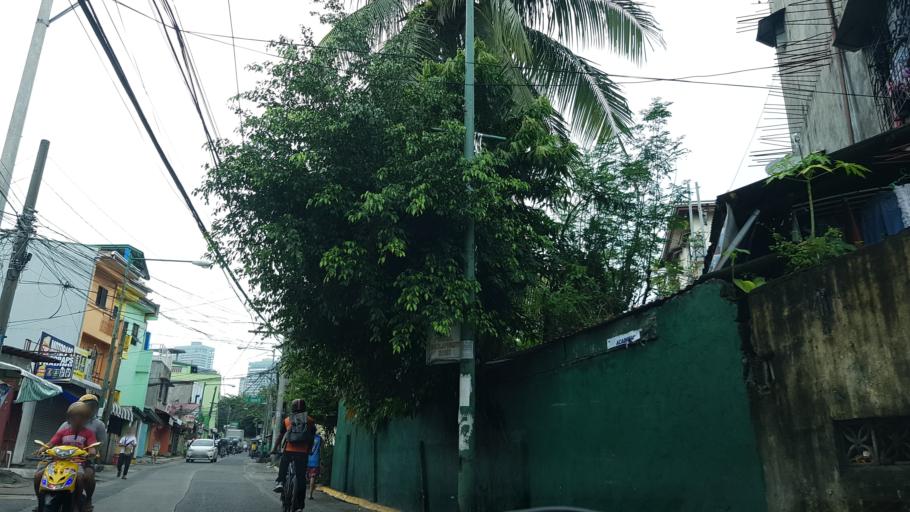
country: PH
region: Calabarzon
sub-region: Province of Rizal
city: Pateros
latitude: 14.5438
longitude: 121.0580
